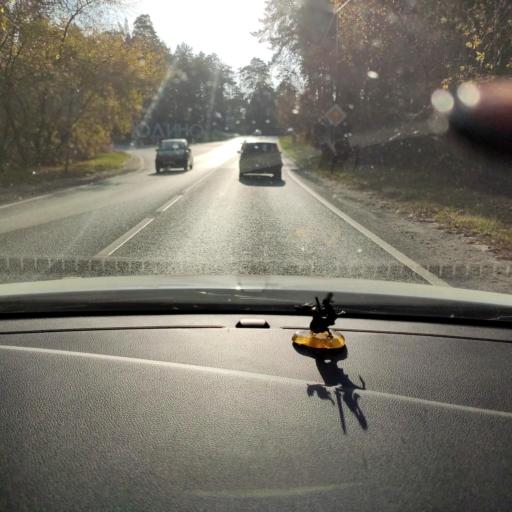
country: RU
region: Tatarstan
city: Osinovo
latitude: 55.8272
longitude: 48.8957
